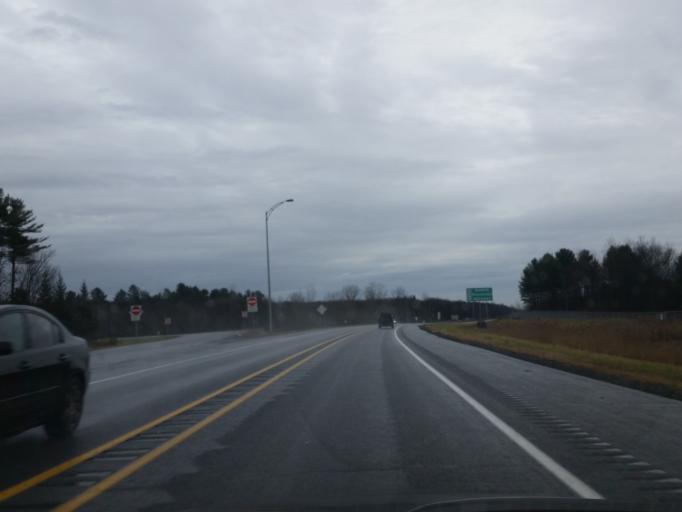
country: CA
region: Quebec
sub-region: Laurentides
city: Mirabel
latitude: 45.6854
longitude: -74.0963
